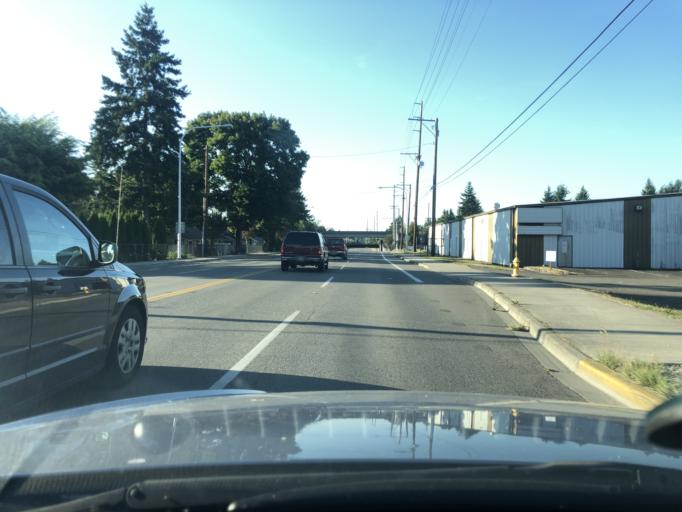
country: US
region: Washington
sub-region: King County
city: Auburn
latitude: 47.3010
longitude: -122.2134
